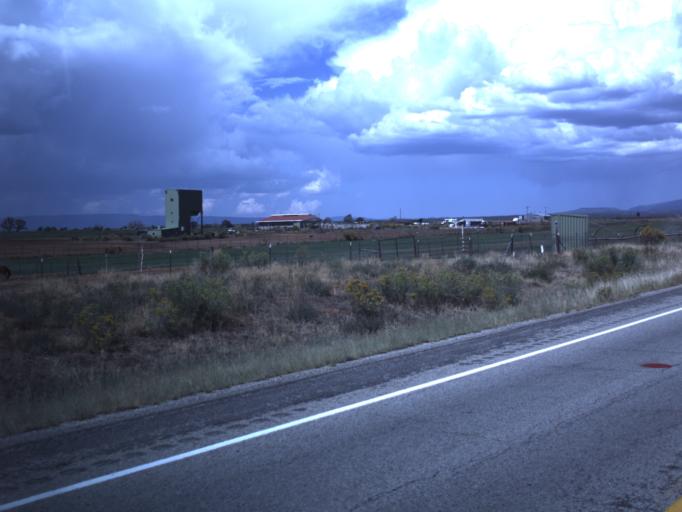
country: US
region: Utah
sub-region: San Juan County
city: Blanding
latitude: 37.5689
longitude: -109.4894
